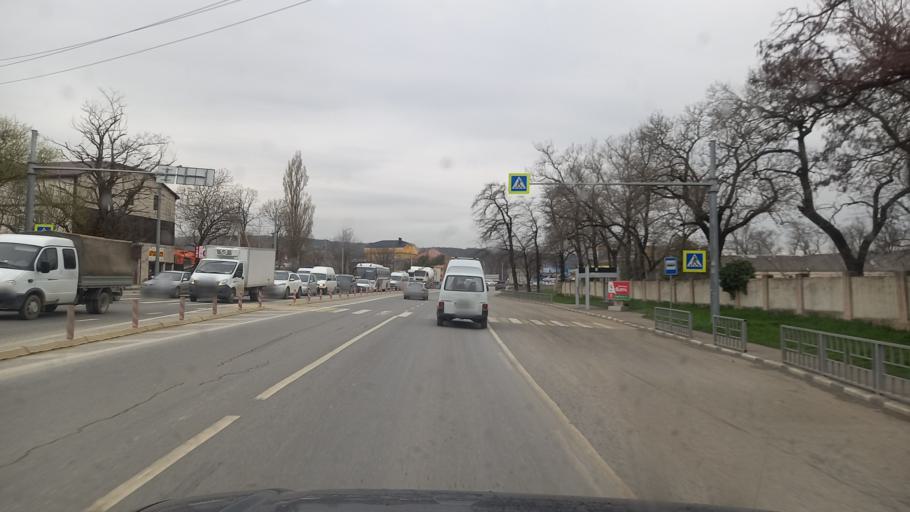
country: RU
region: Krasnodarskiy
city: Gayduk
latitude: 44.7685
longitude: 37.7010
